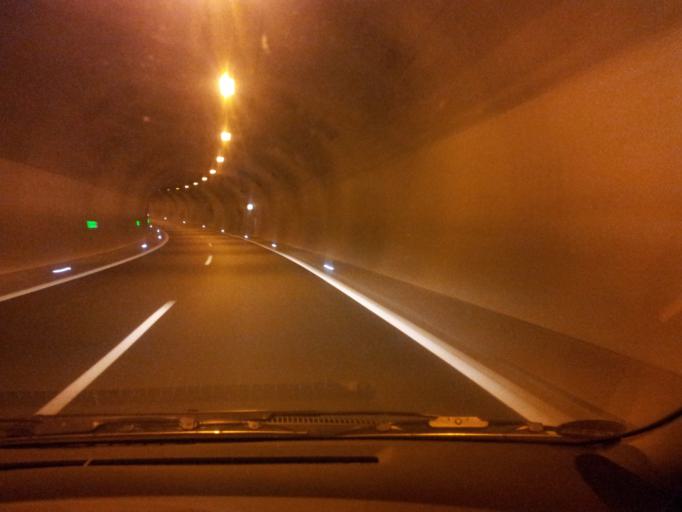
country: DE
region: Baden-Wuerttemberg
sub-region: Regierungsbezirk Stuttgart
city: Leutenbach
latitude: 48.8839
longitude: 9.3966
